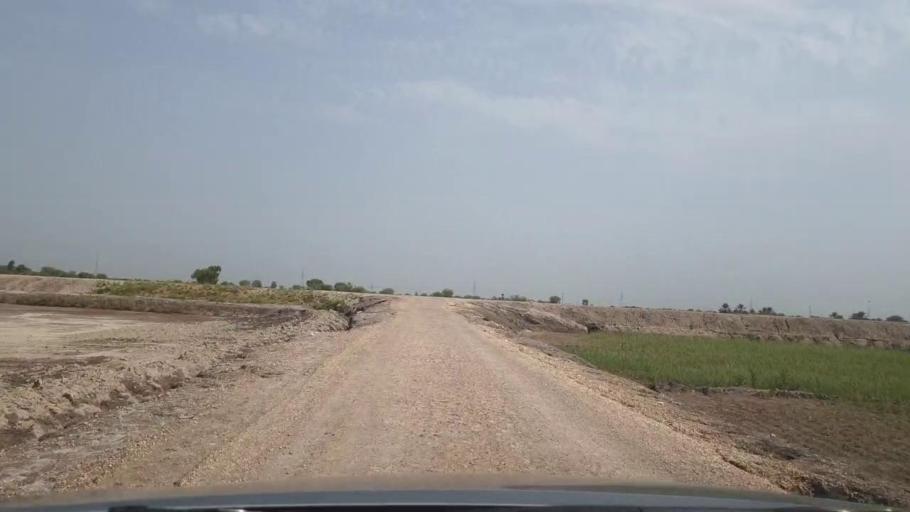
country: PK
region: Sindh
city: Rohri
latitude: 27.6785
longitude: 69.0257
